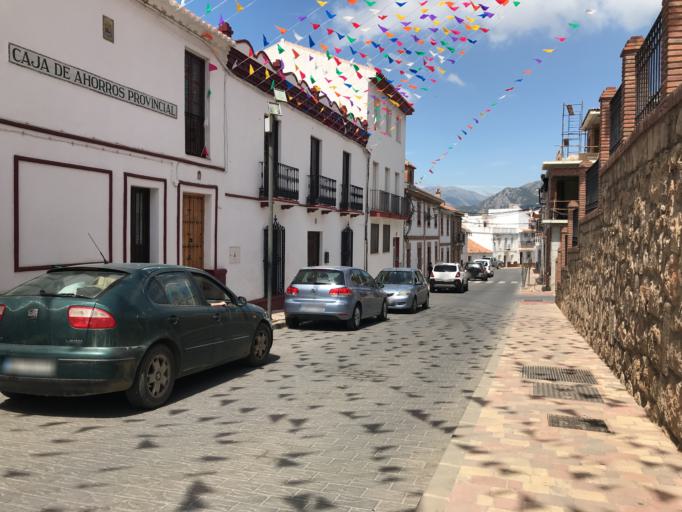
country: ES
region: Andalusia
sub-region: Provincia de Malaga
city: Periana
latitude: 36.9265
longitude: -4.1905
